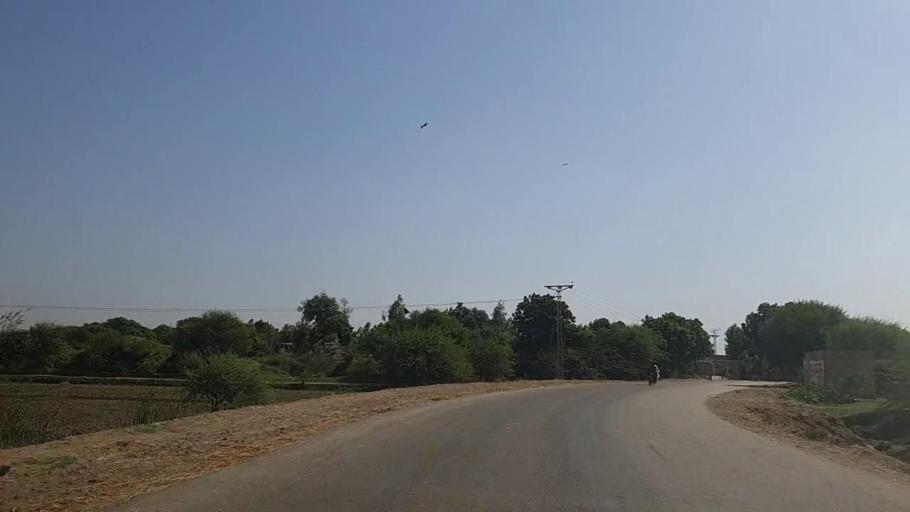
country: PK
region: Sindh
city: Daro Mehar
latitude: 24.7646
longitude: 68.2175
